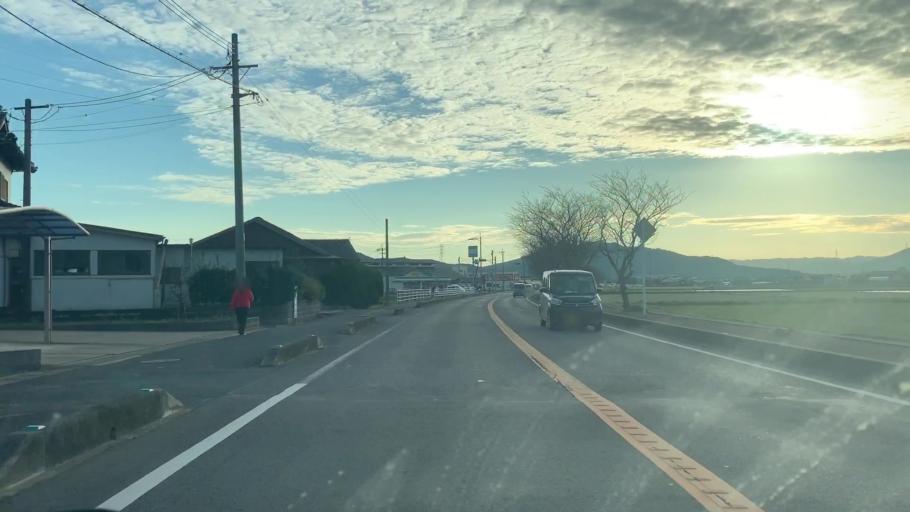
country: JP
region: Saga Prefecture
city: Karatsu
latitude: 33.4107
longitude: 129.9918
